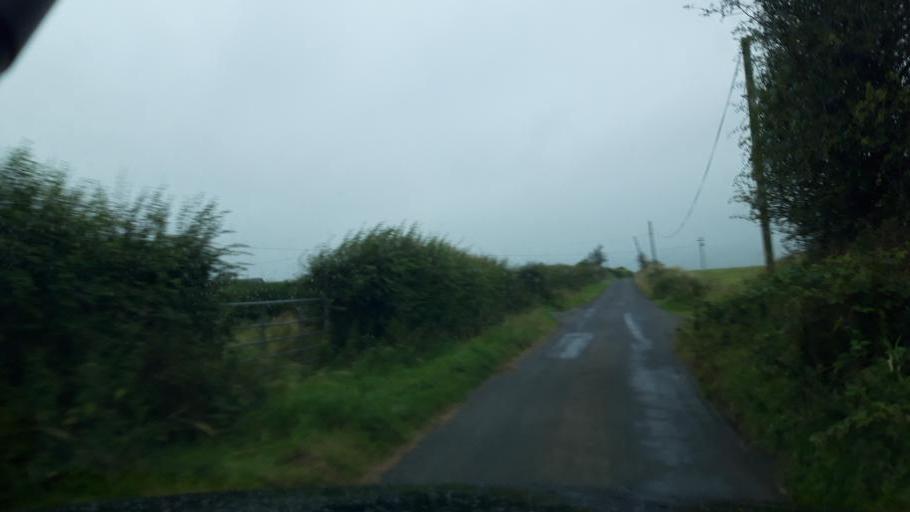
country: IE
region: Leinster
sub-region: Kilkenny
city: Callan
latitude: 52.6338
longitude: -7.5406
